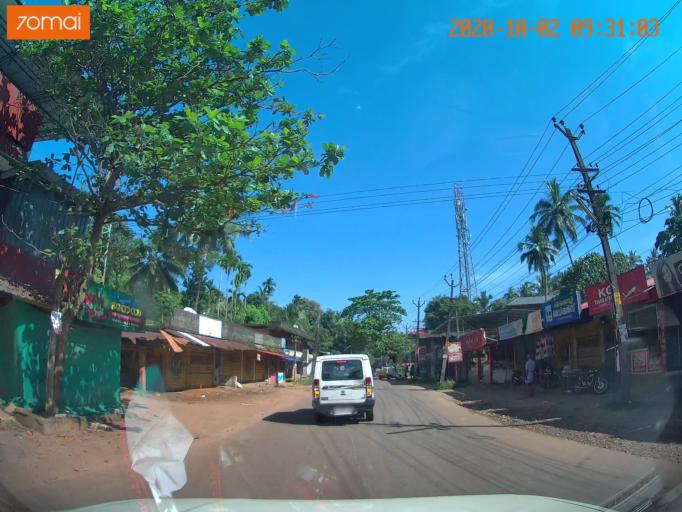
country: IN
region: Kerala
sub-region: Kozhikode
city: Nadapuram
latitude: 11.6217
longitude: 75.7613
